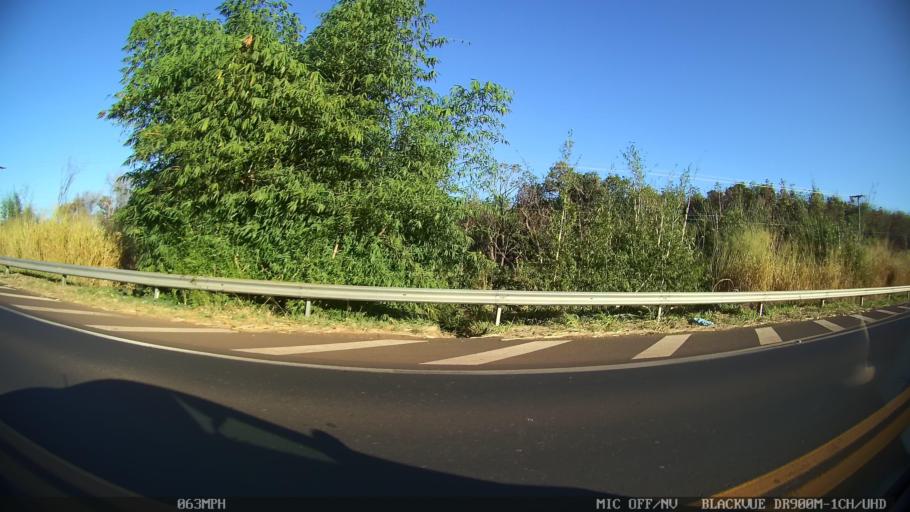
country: BR
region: Sao Paulo
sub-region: Guapiacu
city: Guapiacu
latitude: -20.7666
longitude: -49.1996
